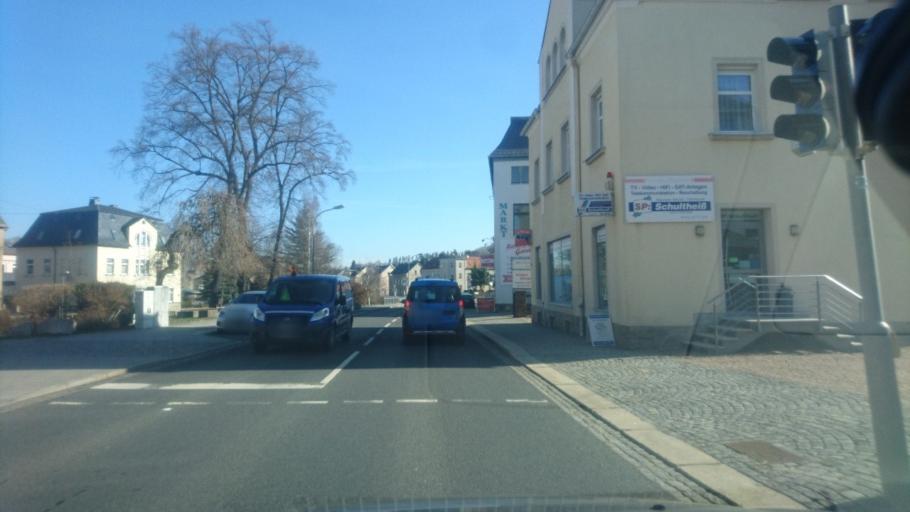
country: DE
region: Saxony
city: Ellefeld
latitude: 50.4837
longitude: 12.3888
